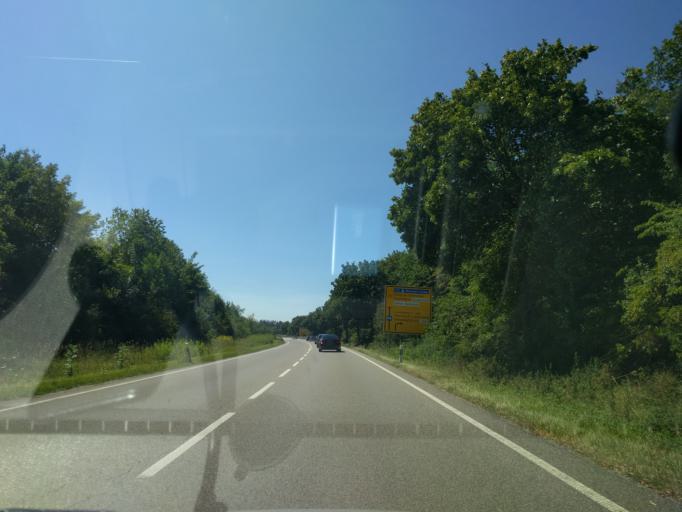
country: DE
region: Bavaria
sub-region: Upper Bavaria
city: Fuerstenfeldbruck
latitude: 48.1807
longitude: 11.2266
